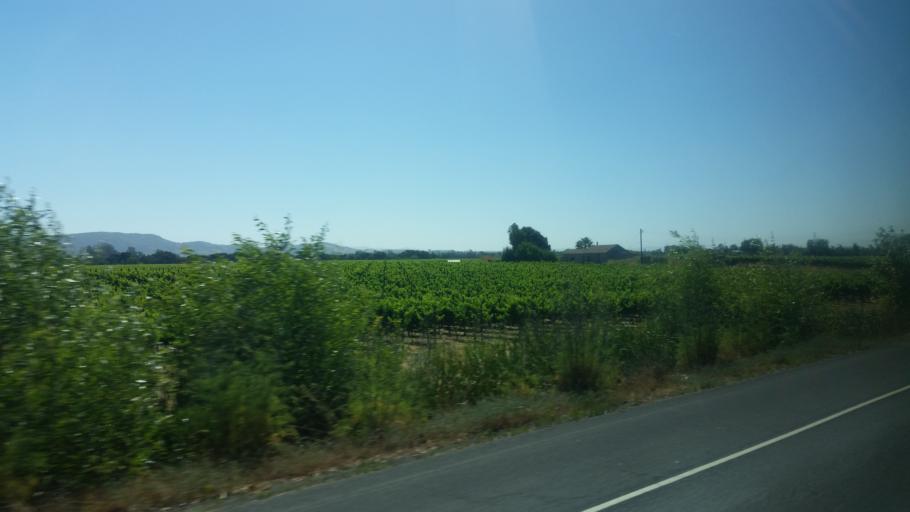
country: US
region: California
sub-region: Sonoma County
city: Temelec
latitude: 38.2574
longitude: -122.4810
